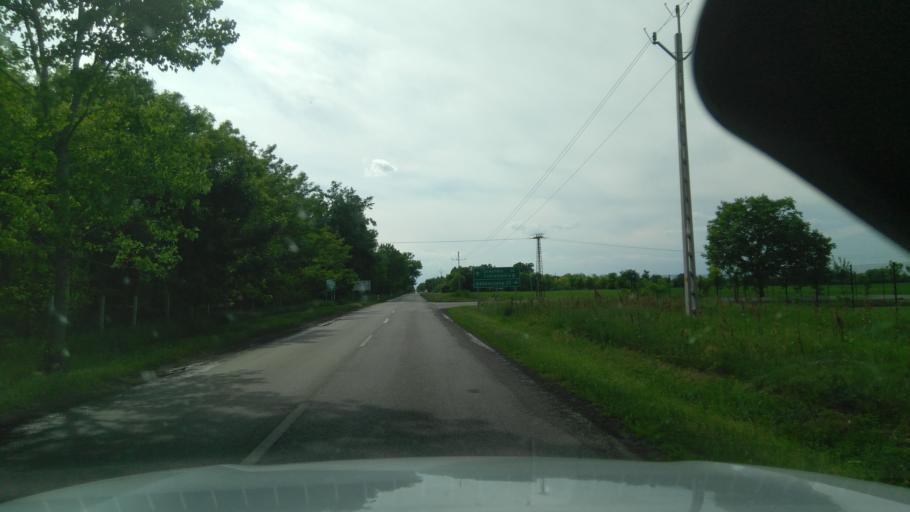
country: HU
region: Bekes
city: Medgyesegyhaza
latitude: 46.5140
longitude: 20.9753
